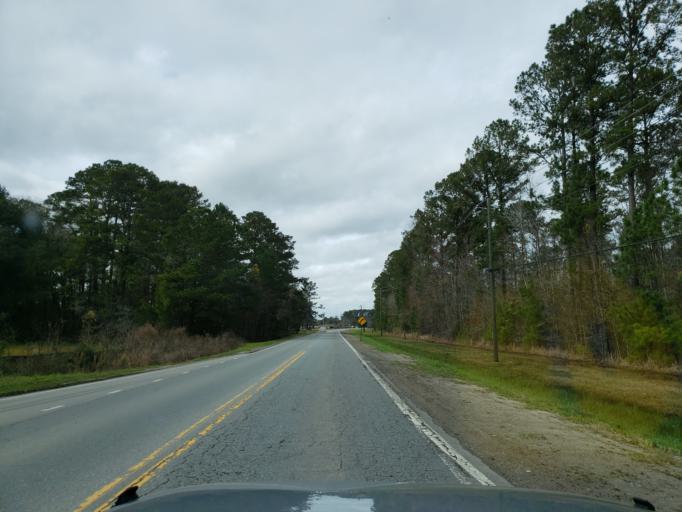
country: US
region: Georgia
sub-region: Chatham County
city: Georgetown
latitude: 32.0160
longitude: -81.2604
